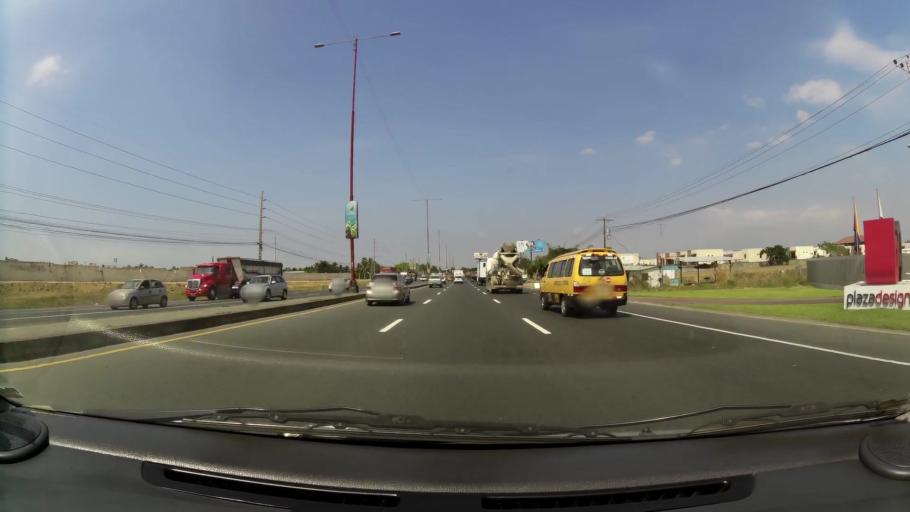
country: EC
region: Guayas
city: El Triunfo
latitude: -2.0501
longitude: -79.9035
